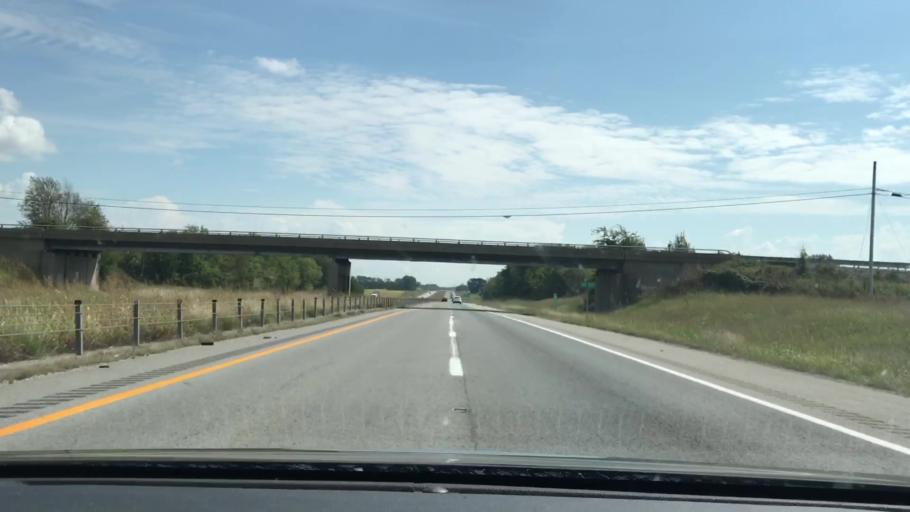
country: US
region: Kentucky
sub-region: Christian County
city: Hopkinsville
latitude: 36.7550
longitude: -87.5301
